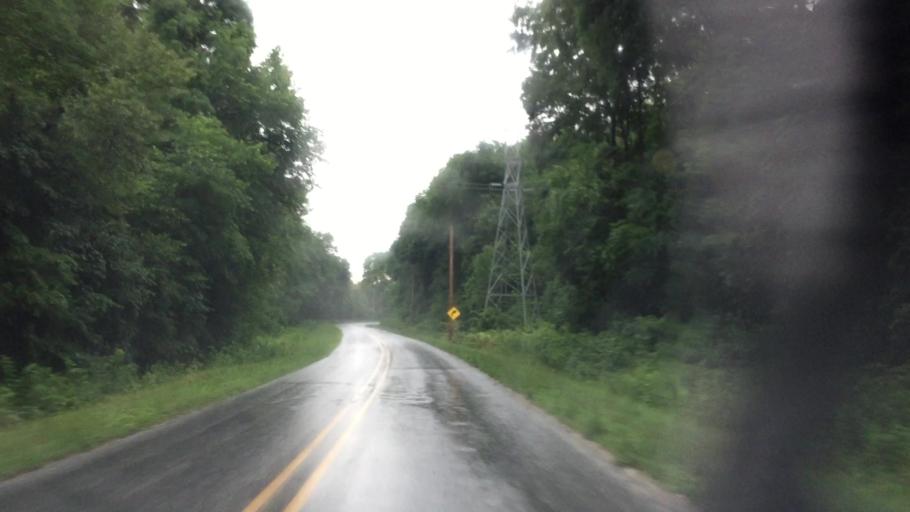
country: US
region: Iowa
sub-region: Lee County
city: Fort Madison
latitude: 40.6093
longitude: -91.2803
